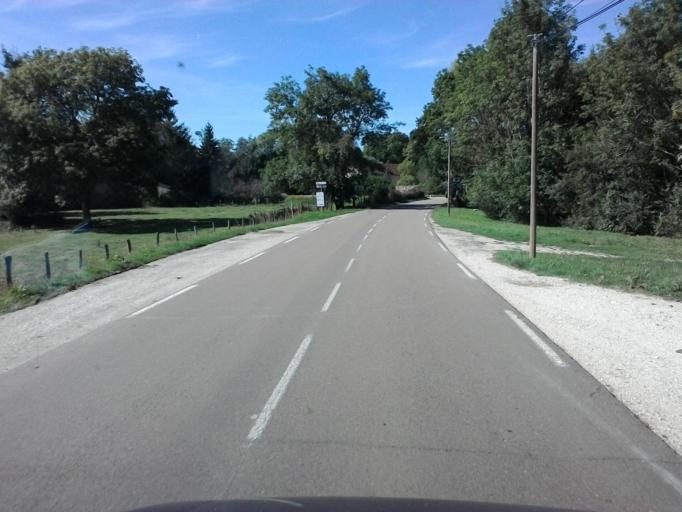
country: FR
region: Bourgogne
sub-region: Departement de l'Yonne
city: Tonnerre
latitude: 47.7504
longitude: 3.9190
